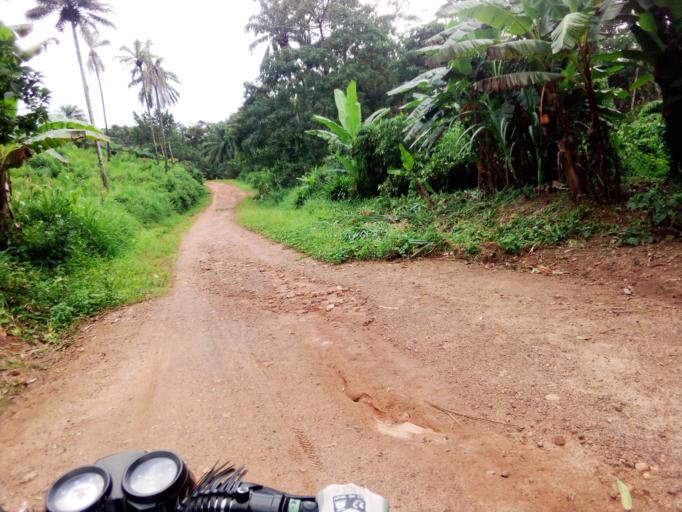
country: SL
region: Eastern Province
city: Giehun
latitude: 8.5622
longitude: -10.9962
